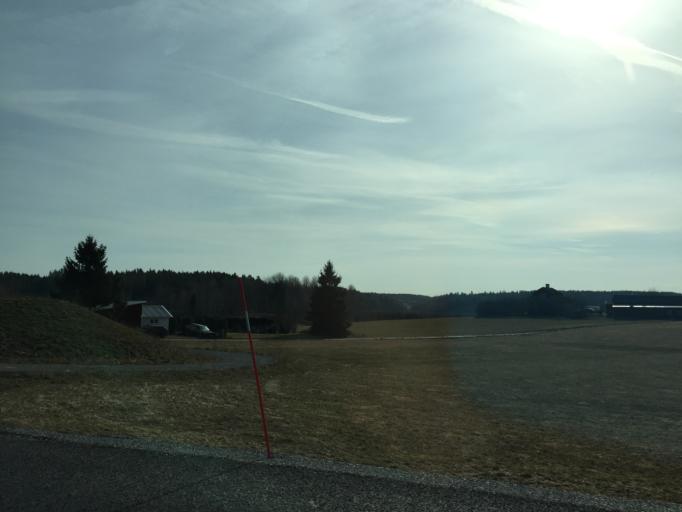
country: SE
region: Soedermanland
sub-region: Flens Kommun
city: Halleforsnas
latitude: 59.0299
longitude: 16.4174
